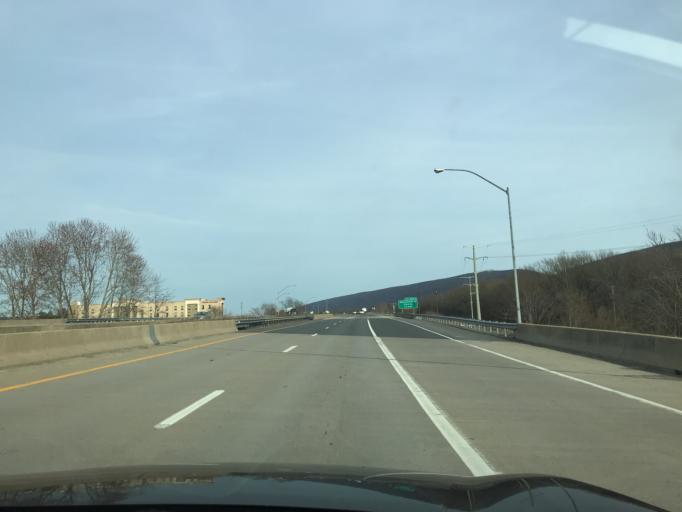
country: US
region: Pennsylvania
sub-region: Lycoming County
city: Faxon
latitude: 41.2487
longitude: -76.9766
